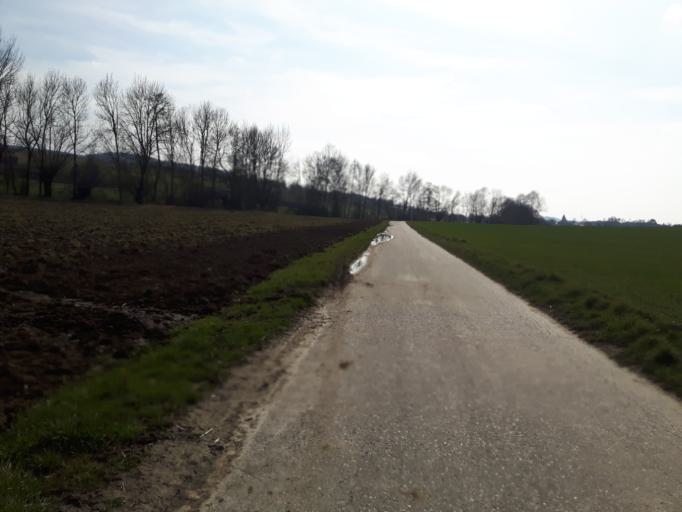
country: DE
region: Baden-Wuerttemberg
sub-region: Regierungsbezirk Stuttgart
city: Schwaigern
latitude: 49.1364
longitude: 9.0227
